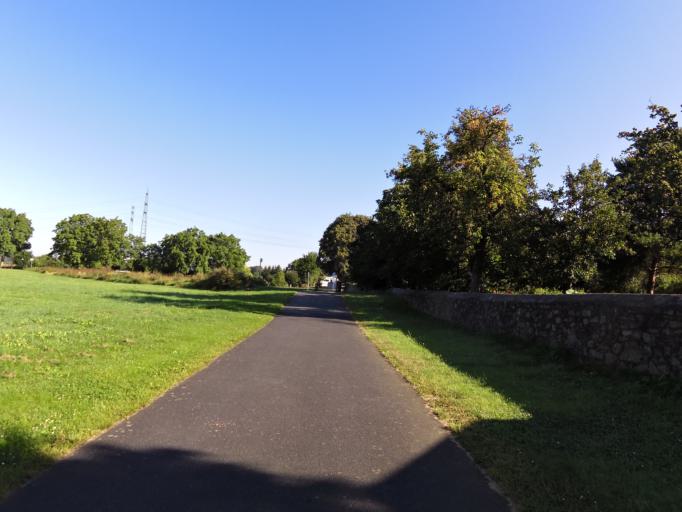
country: DE
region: Saxony
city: Weissig
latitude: 51.2400
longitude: 13.4143
